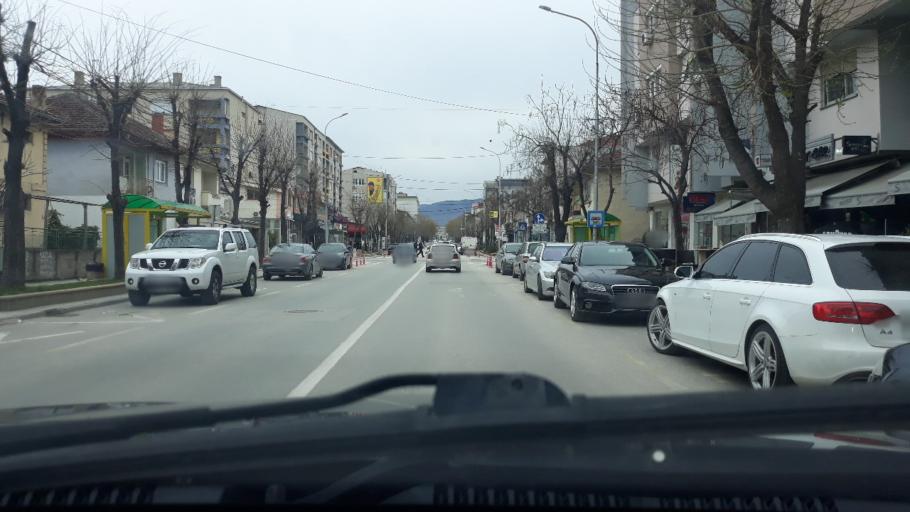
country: MK
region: Kavadarci
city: Kavadarci
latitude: 41.4382
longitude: 22.0104
